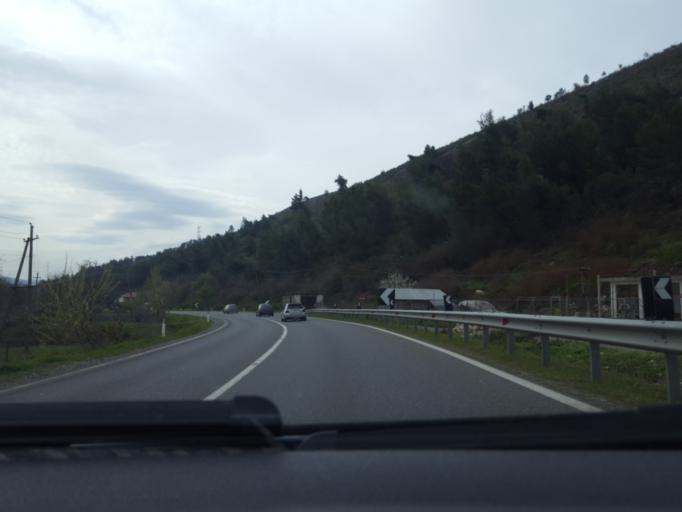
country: AL
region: Lezhe
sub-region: Rrethi i Lezhes
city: Balldreni i Ri
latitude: 41.8016
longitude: 19.6302
